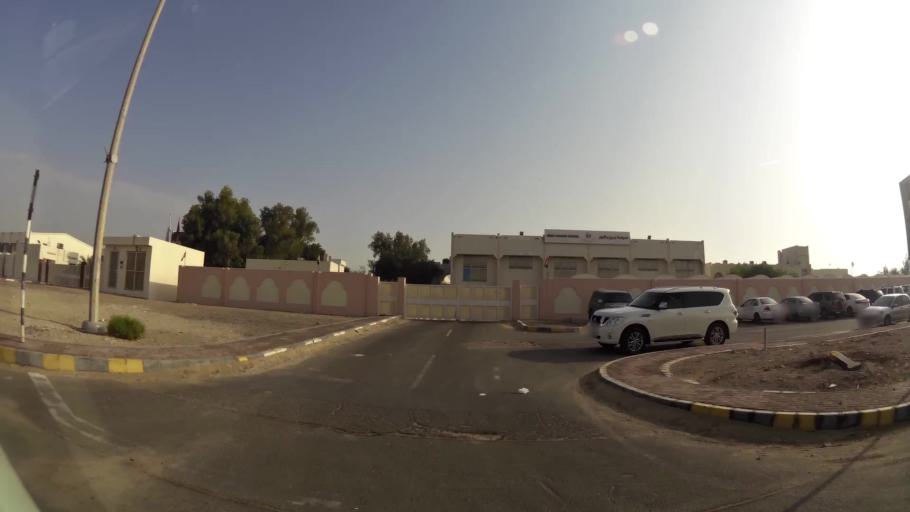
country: AE
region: Abu Dhabi
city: Abu Dhabi
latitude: 24.2972
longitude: 54.6189
